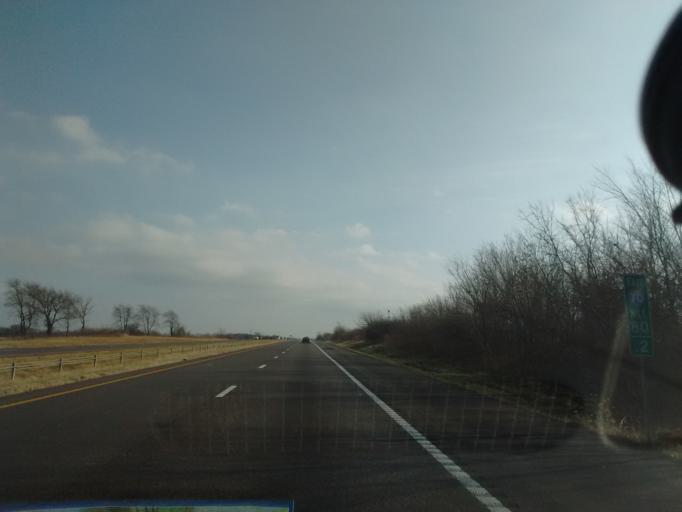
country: US
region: Missouri
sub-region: Saline County
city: Marshall
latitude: 38.9582
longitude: -93.1676
